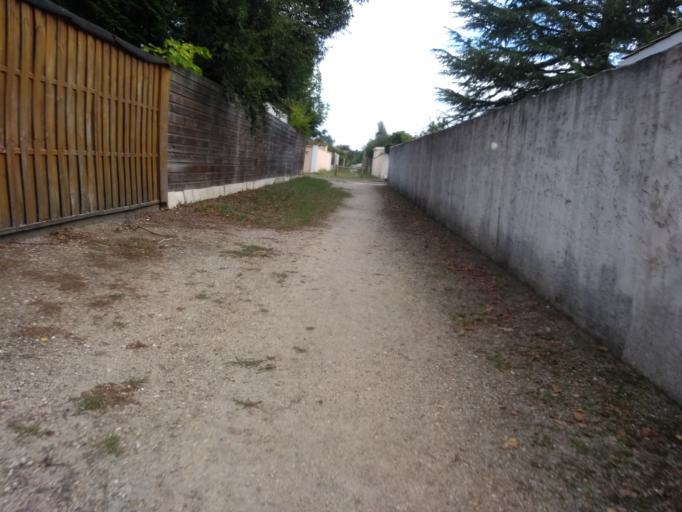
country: FR
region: Aquitaine
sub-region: Departement de la Gironde
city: Saint-Aubin-de-Medoc
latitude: 44.7671
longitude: -0.6993
